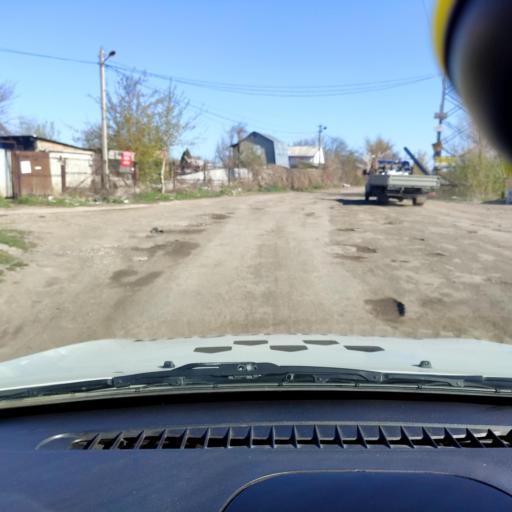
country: RU
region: Samara
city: Tol'yatti
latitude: 53.5823
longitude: 49.2939
